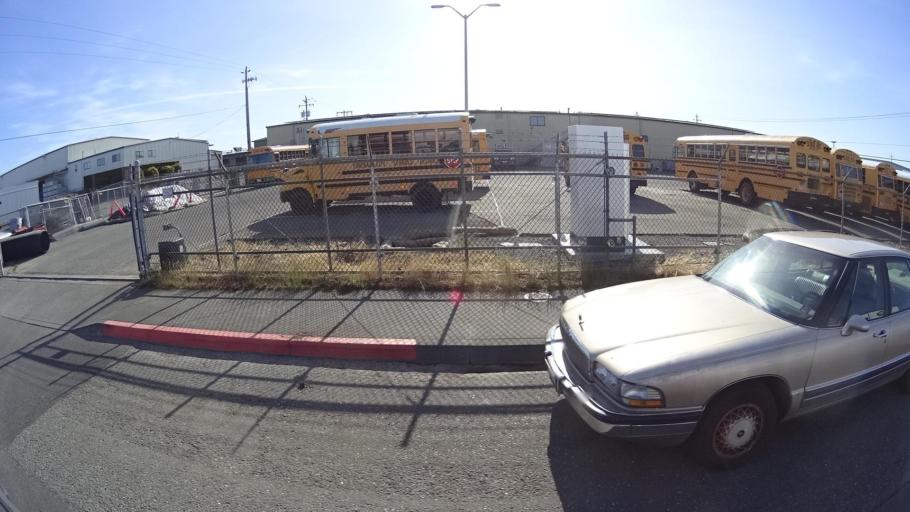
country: US
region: California
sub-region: Humboldt County
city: Eureka
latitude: 40.7945
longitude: -124.1791
